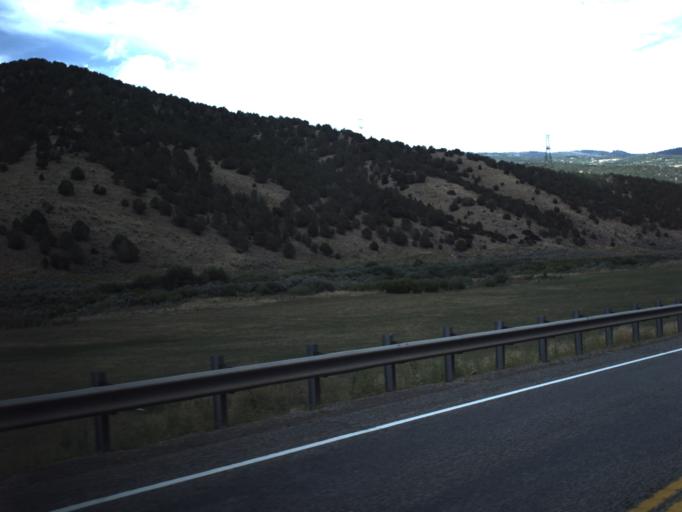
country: US
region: Utah
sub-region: Utah County
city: Woodland Hills
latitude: 39.8778
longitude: -111.5413
